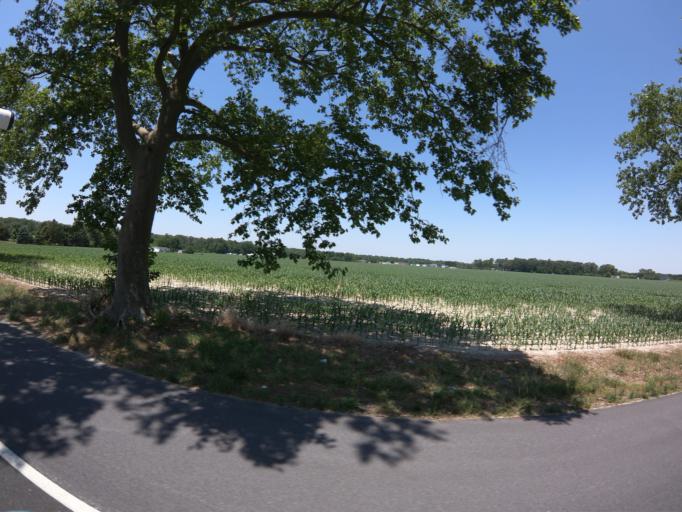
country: US
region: Delaware
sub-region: Kent County
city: Harrington
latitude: 38.9250
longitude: -75.5450
